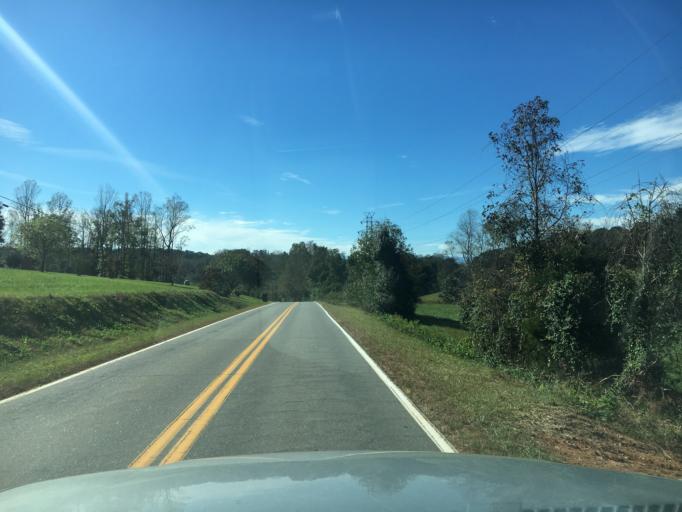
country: US
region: North Carolina
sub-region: Burke County
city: Salem
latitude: 35.7205
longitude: -81.7196
